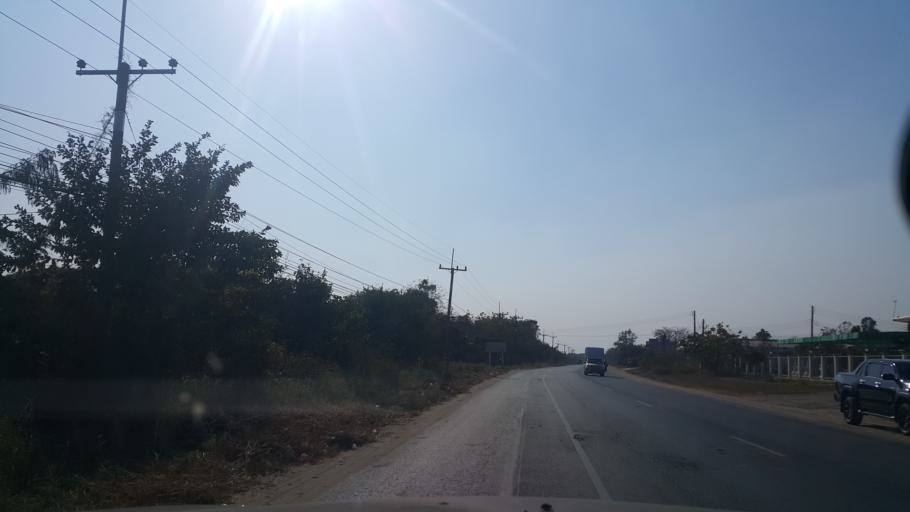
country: TH
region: Nakhon Ratchasima
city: Phimai
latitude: 15.2135
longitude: 102.4789
